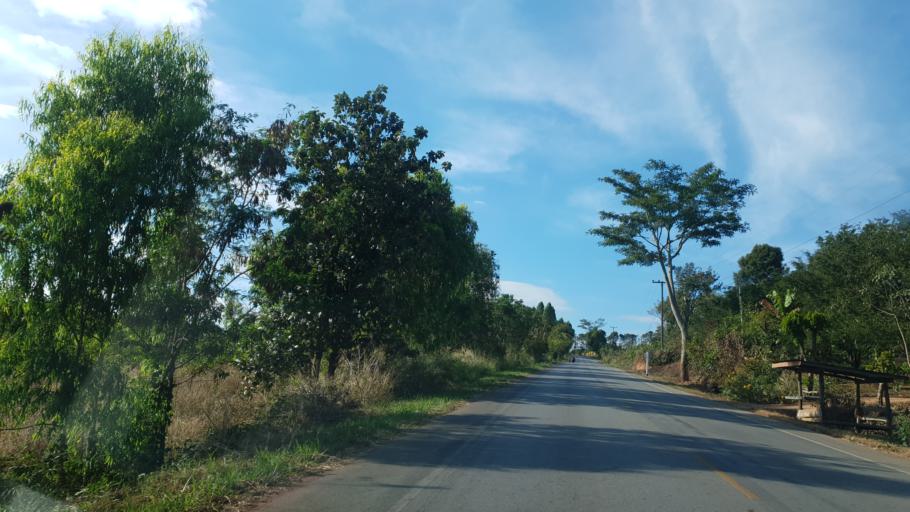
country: TH
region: Loei
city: Phu Ruea
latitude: 17.4432
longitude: 101.5013
